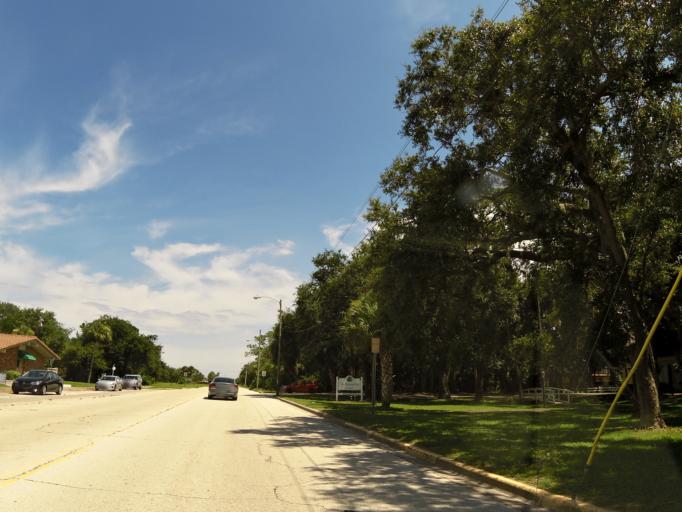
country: US
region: Florida
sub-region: Volusia County
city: Daytona Beach
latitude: 29.1945
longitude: -81.0114
